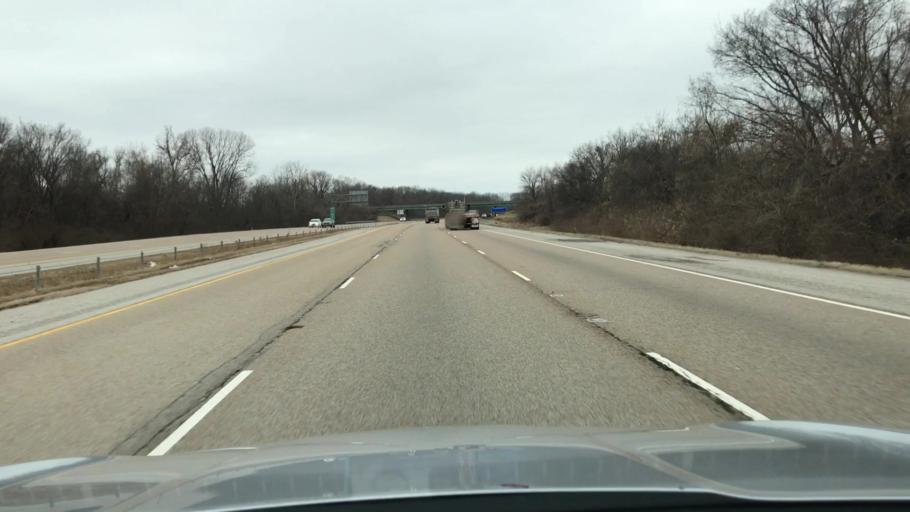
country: US
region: Illinois
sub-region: Saint Clair County
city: Fairmont City
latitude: 38.6639
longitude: -90.0622
